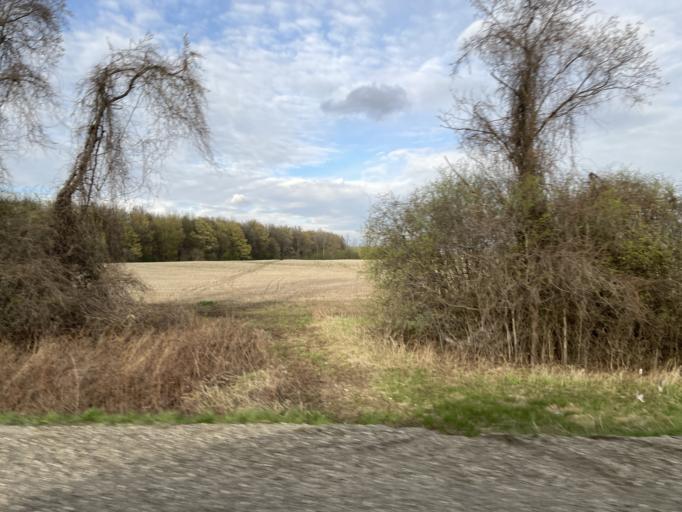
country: CA
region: Ontario
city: Waterloo
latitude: 43.4754
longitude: -80.4025
